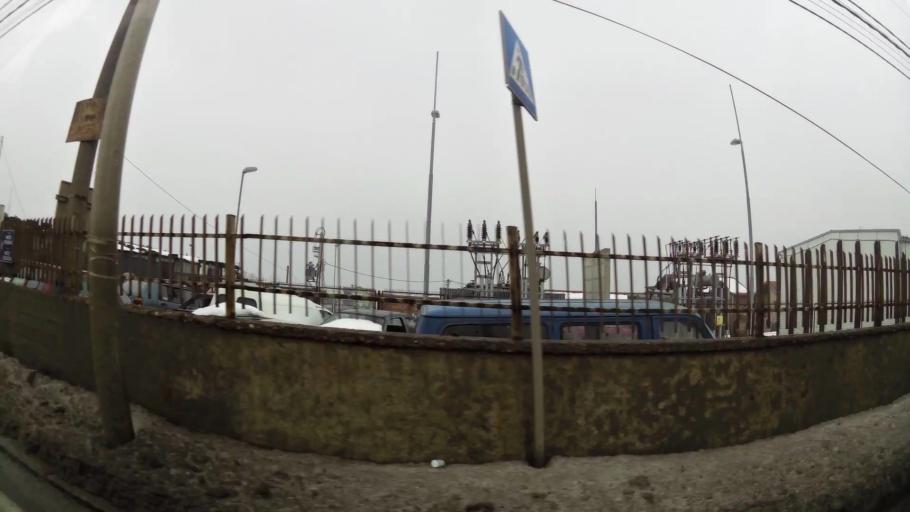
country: RS
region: Central Serbia
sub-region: Belgrade
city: Zvezdara
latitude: 44.7675
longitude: 20.5338
